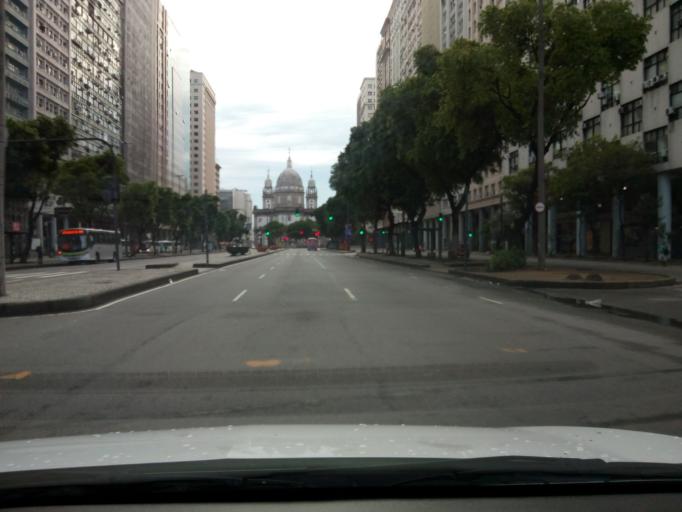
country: BR
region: Rio de Janeiro
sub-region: Rio De Janeiro
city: Rio de Janeiro
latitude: -22.9022
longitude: -43.1814
